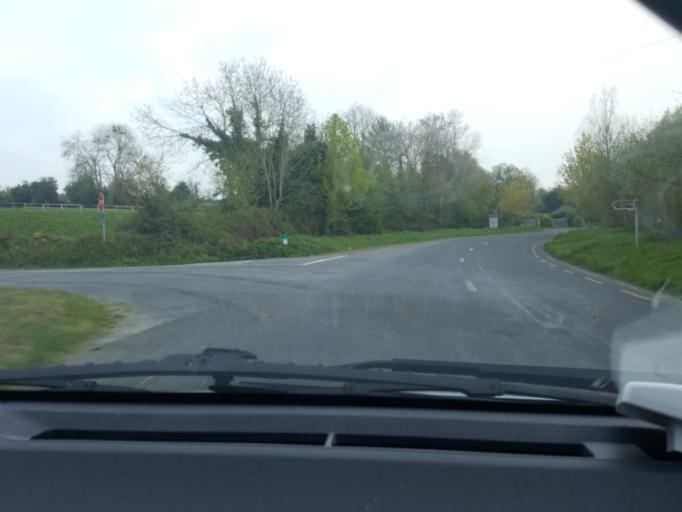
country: IE
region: Munster
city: Cahir
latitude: 52.3880
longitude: -7.9115
